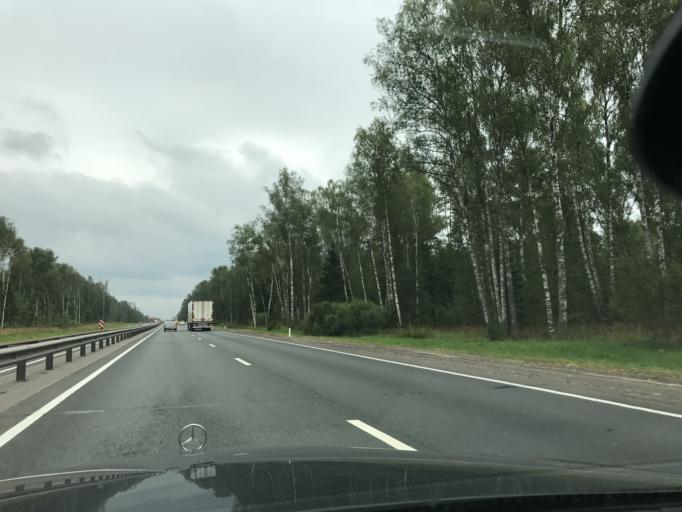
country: RU
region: Vladimir
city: Kameshkovo
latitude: 56.1991
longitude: 41.0492
